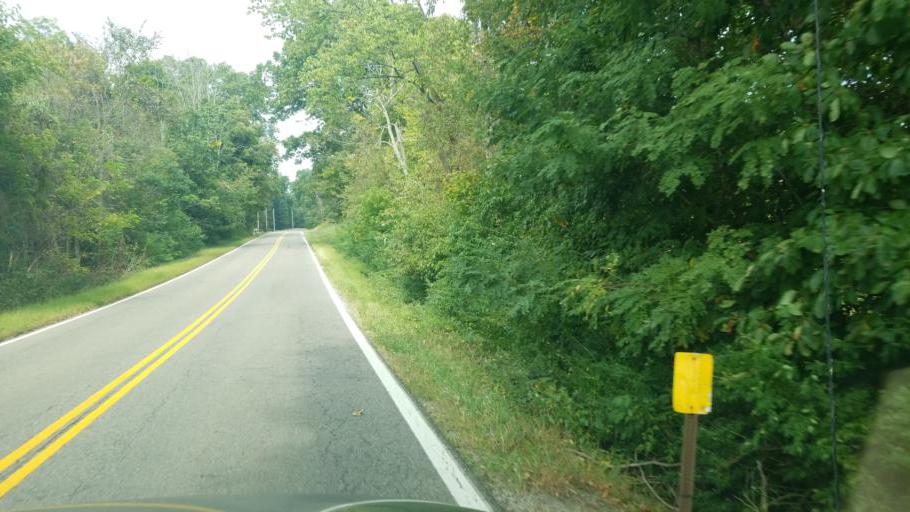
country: US
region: Ohio
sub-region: Licking County
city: Newark
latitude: 39.9822
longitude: -82.2640
